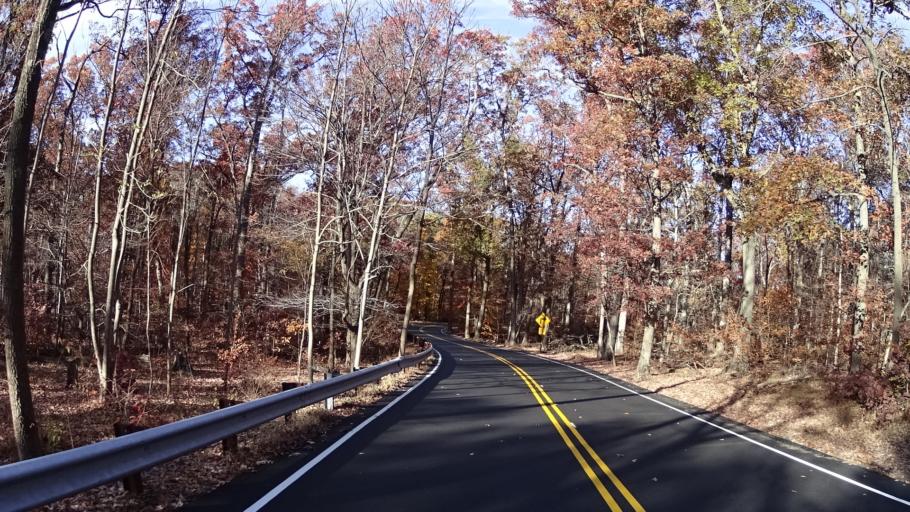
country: US
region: New Jersey
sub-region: Union County
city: Scotch Plains
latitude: 40.6648
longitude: -74.3987
